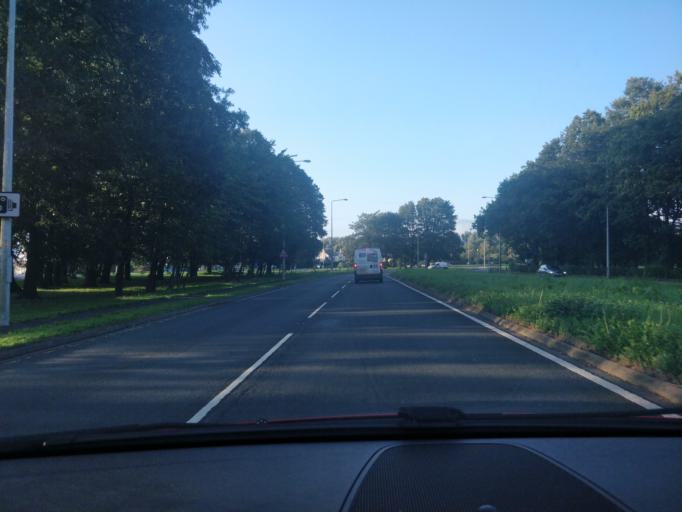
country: GB
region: England
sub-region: Lancashire
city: Preston
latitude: 53.7339
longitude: -2.7594
